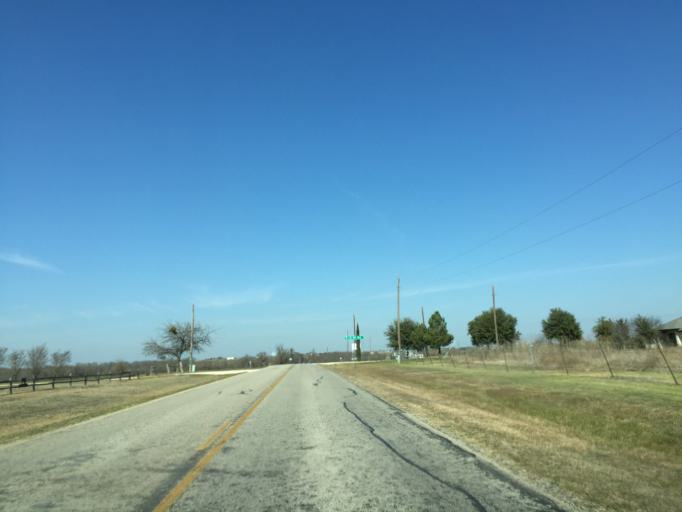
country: US
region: Texas
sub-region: Williamson County
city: Georgetown
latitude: 30.6813
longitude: -97.5887
